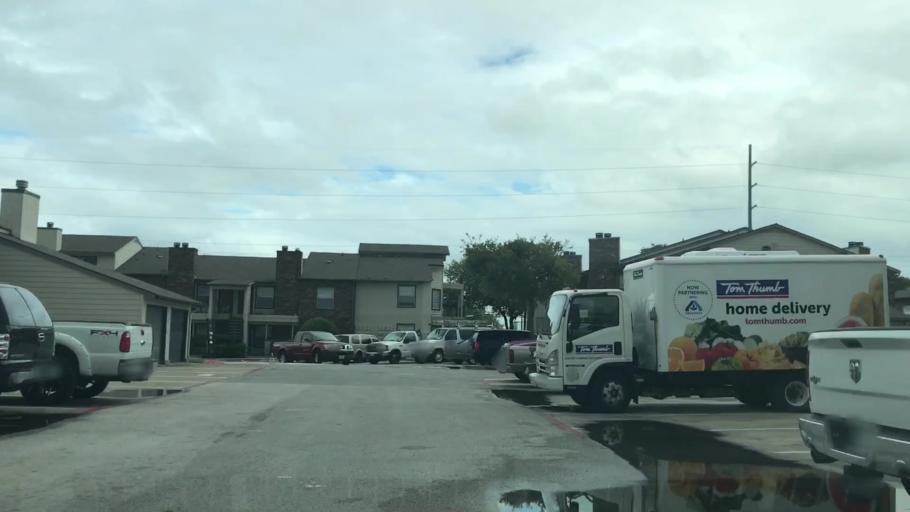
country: US
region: Texas
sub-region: Dallas County
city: Garland
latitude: 32.8827
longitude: -96.6184
